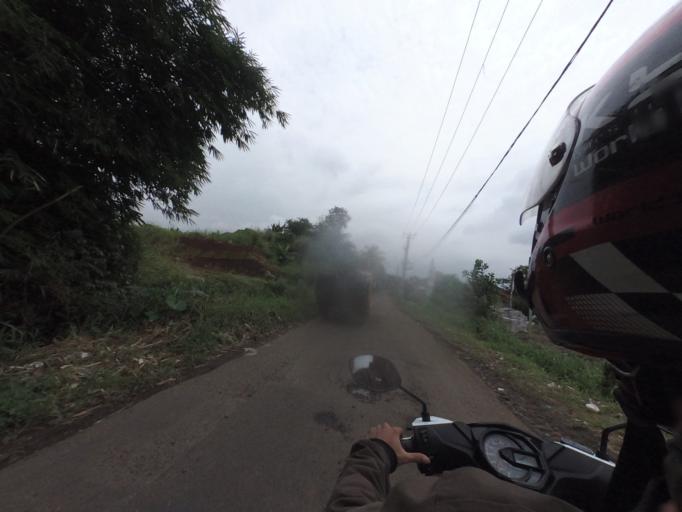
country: ID
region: West Java
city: Bogor
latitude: -6.6151
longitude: 106.7503
